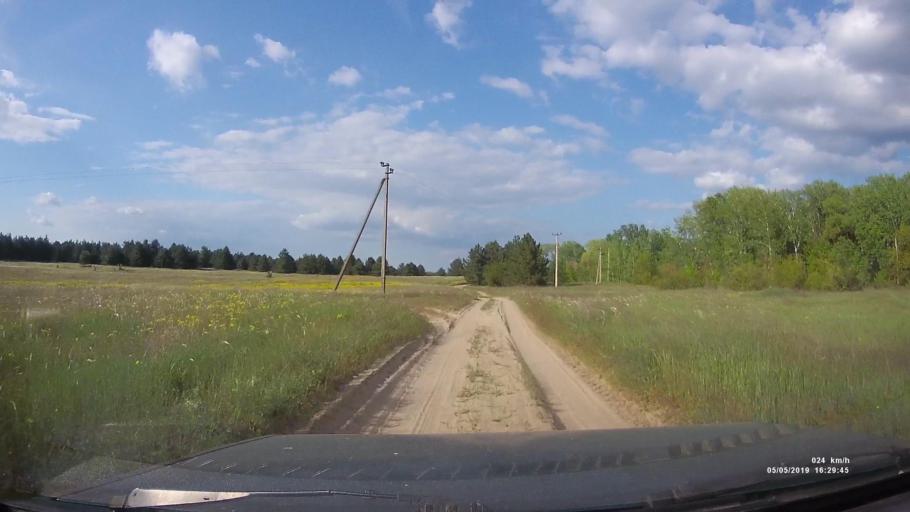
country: RU
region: Rostov
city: Ust'-Donetskiy
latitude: 47.7714
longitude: 41.0146
